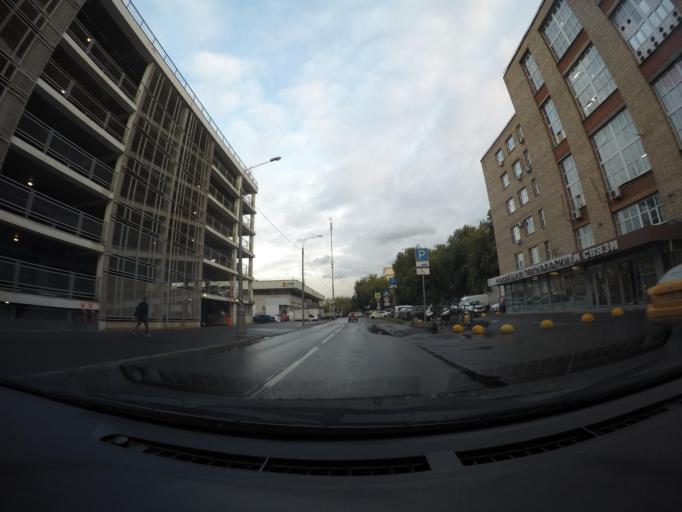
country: RU
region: Moscow
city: Sokol'niki
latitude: 55.7989
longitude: 37.6961
